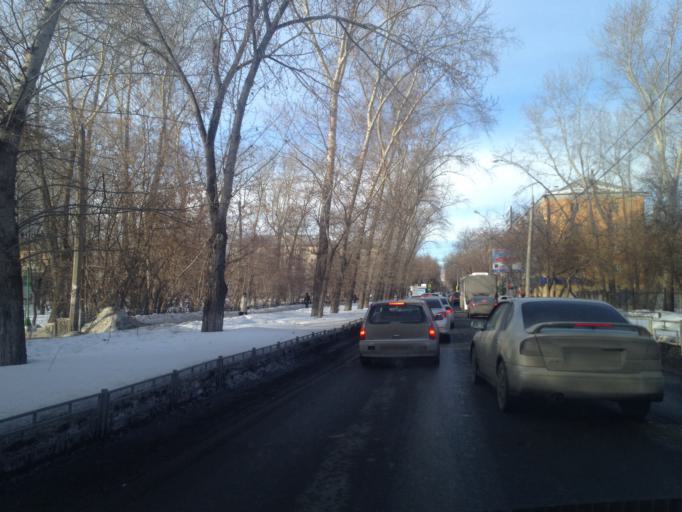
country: RU
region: Sverdlovsk
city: Yekaterinburg
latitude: 56.8354
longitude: 60.6281
